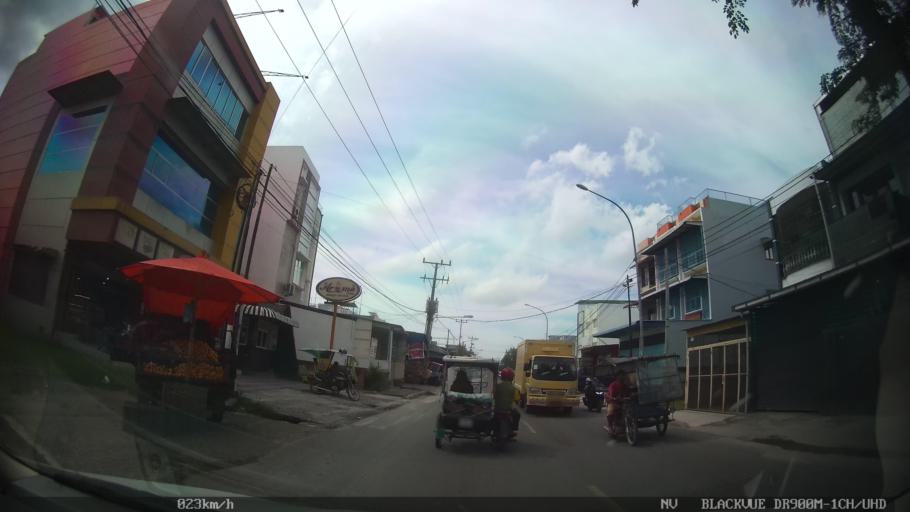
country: ID
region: North Sumatra
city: Percut
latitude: 3.5669
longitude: 98.8722
